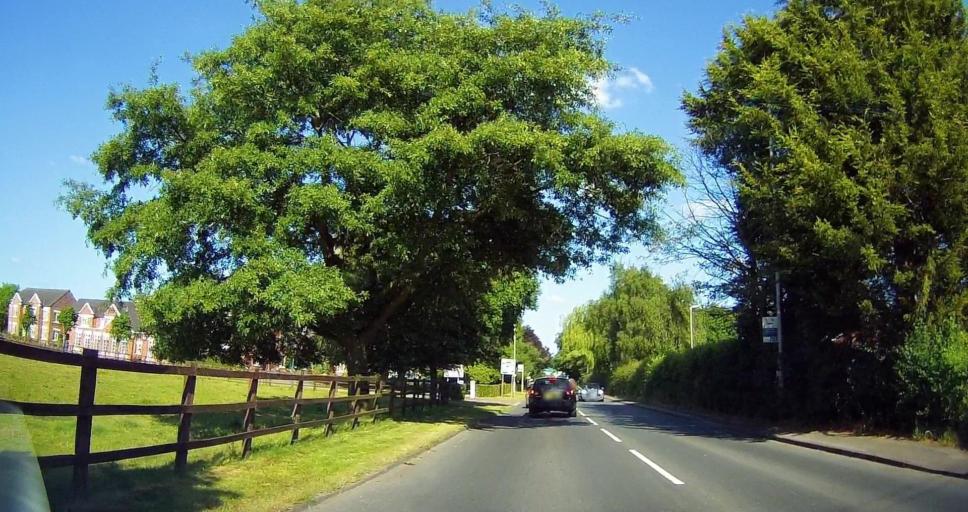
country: GB
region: England
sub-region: Cheshire East
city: Sandbach
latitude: 53.1517
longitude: -2.3524
